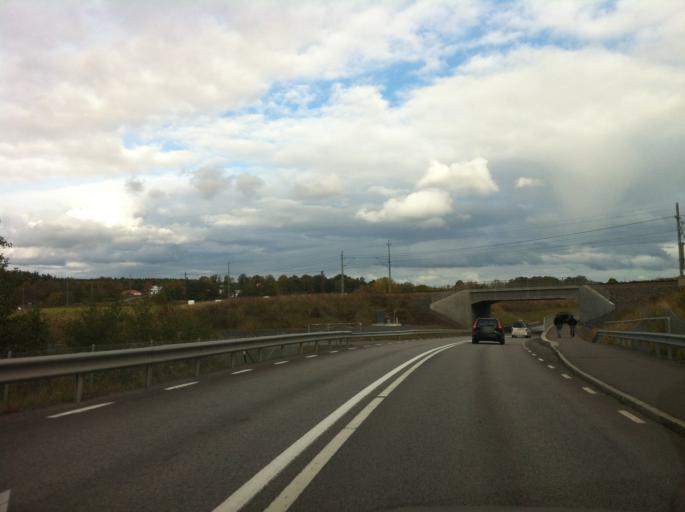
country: SE
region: OEstergoetland
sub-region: Motala Kommun
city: Motala
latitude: 58.5021
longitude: 15.0141
